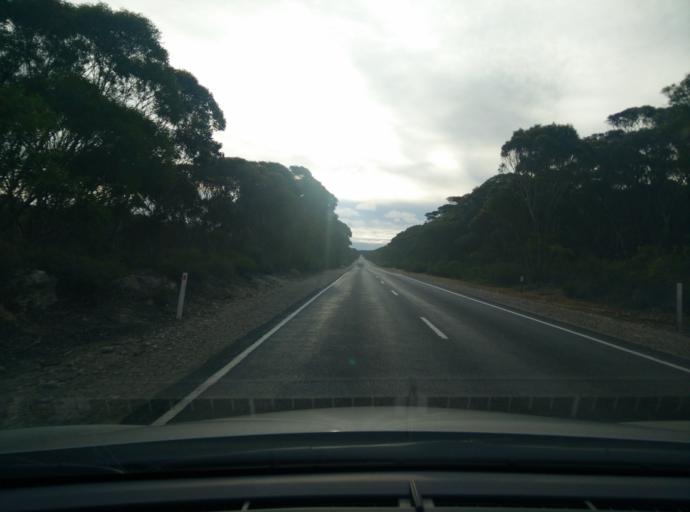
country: AU
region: South Australia
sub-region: Kangaroo Island
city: Kingscote
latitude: -35.7995
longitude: 137.8443
